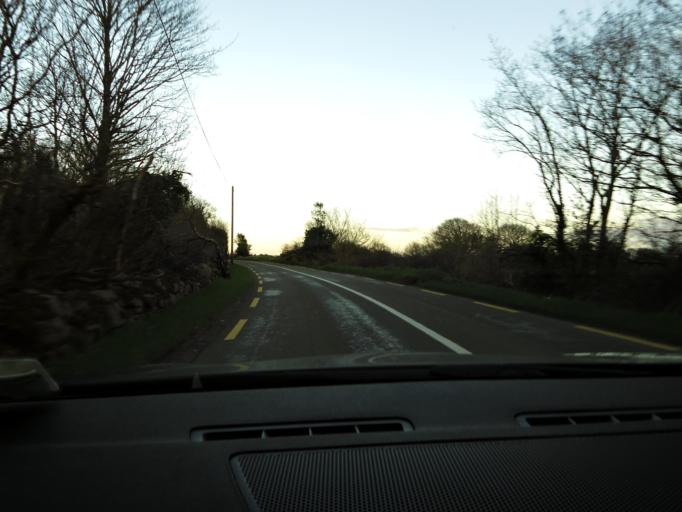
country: IE
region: Connaught
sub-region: Sligo
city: Ballymote
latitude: 53.9732
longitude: -8.4471
